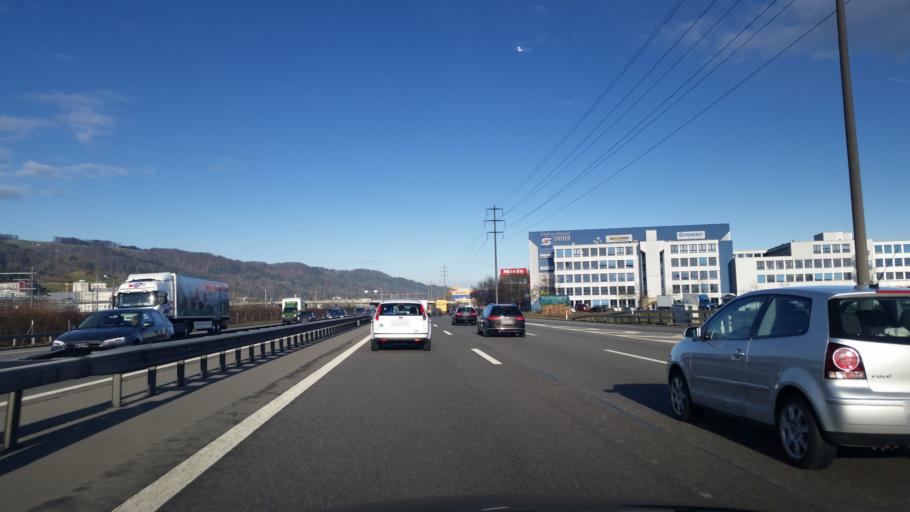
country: CH
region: Aargau
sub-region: Bezirk Baden
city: Spreitenbach
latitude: 47.4266
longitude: 8.3750
